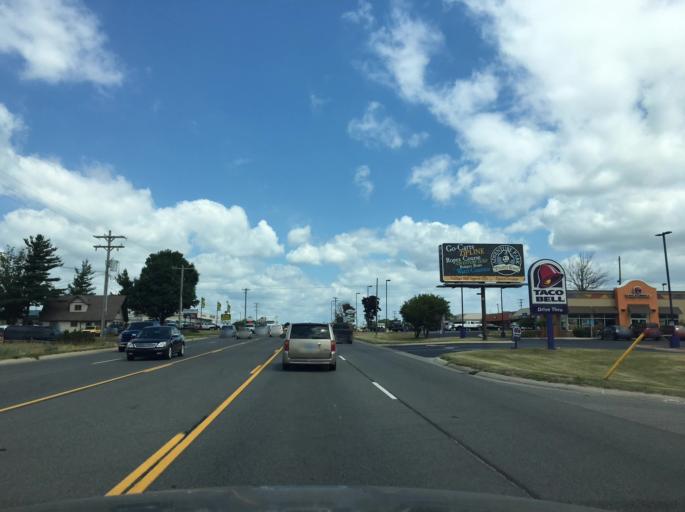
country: US
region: Michigan
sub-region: Grand Traverse County
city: Traverse City
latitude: 44.6748
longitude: -85.6563
